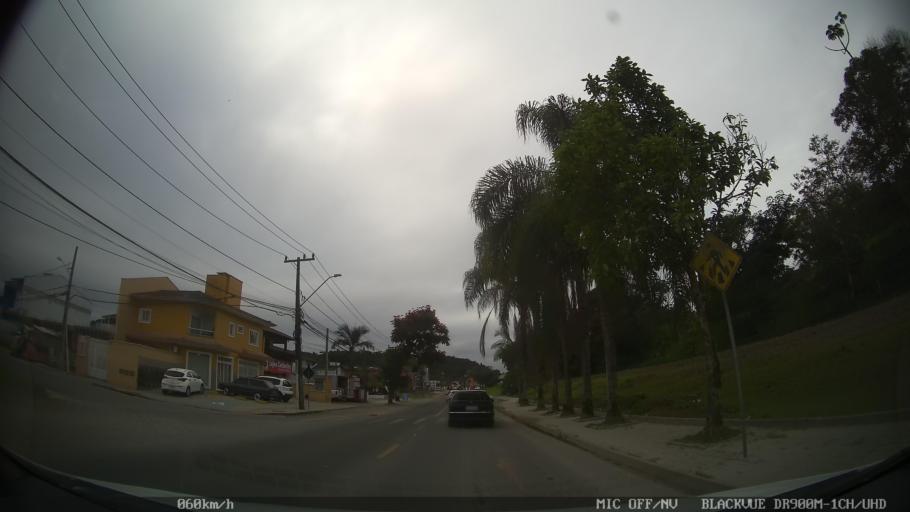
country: BR
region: Santa Catarina
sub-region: Joinville
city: Joinville
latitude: -26.3363
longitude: -48.8784
